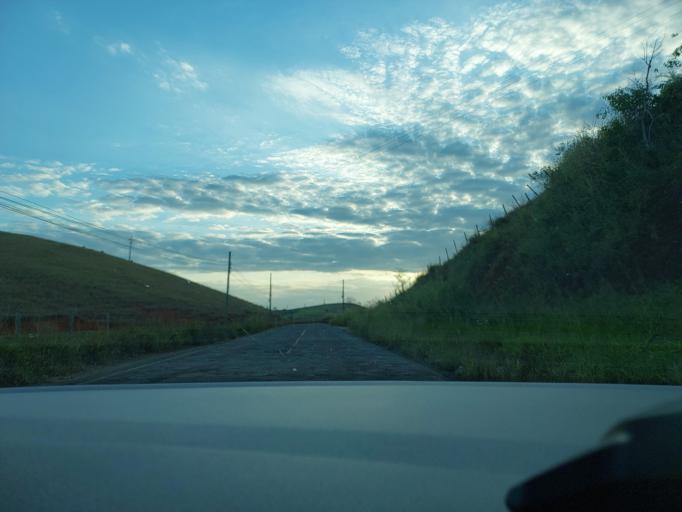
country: BR
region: Rio de Janeiro
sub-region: Natividade
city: Natividade
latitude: -21.1914
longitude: -42.1097
